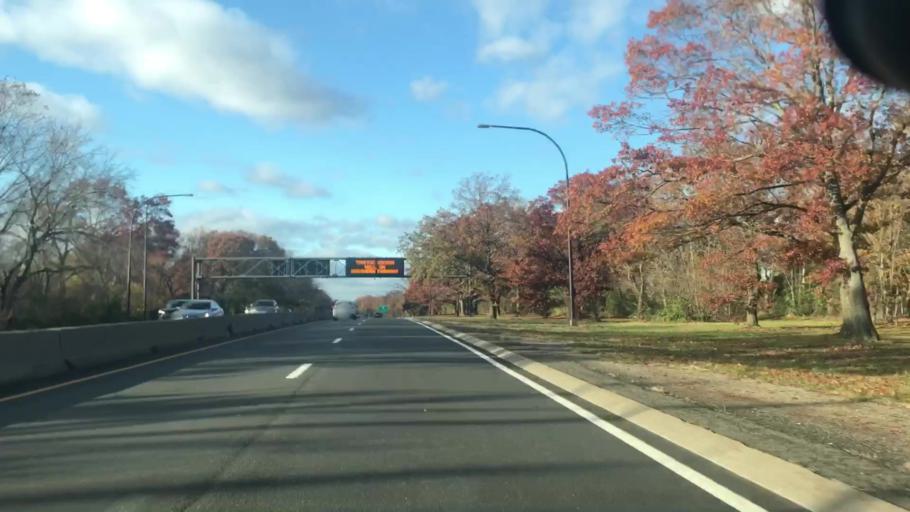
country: US
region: New York
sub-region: Nassau County
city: North Bellmore
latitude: 40.7106
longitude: -73.5279
